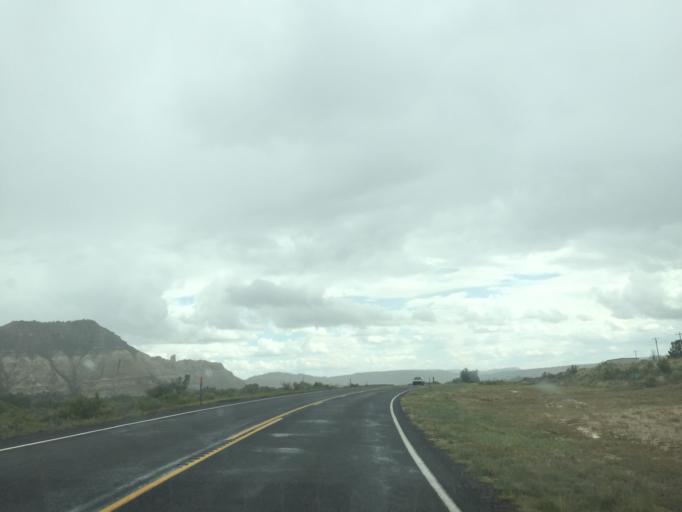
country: US
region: Utah
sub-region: Garfield County
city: Panguitch
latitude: 37.5866
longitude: -112.0580
